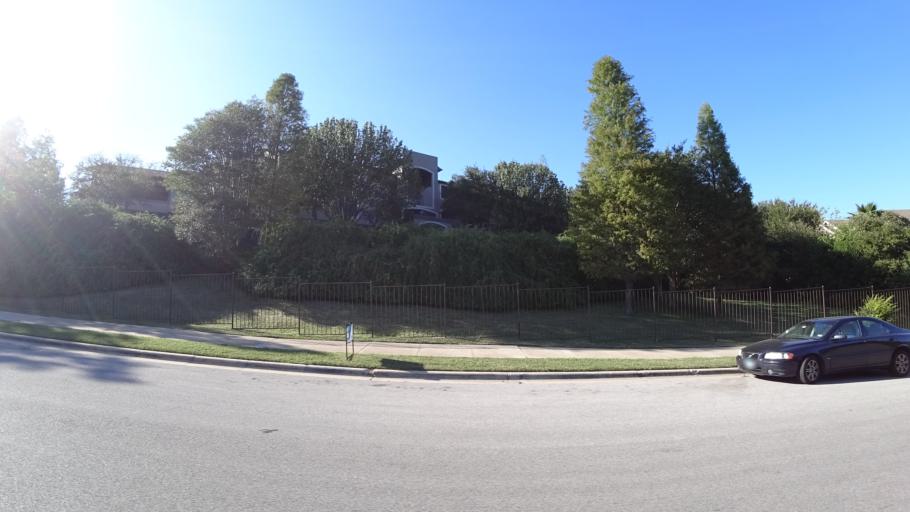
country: US
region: Texas
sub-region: Travis County
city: Austin
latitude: 30.2226
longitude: -97.7231
